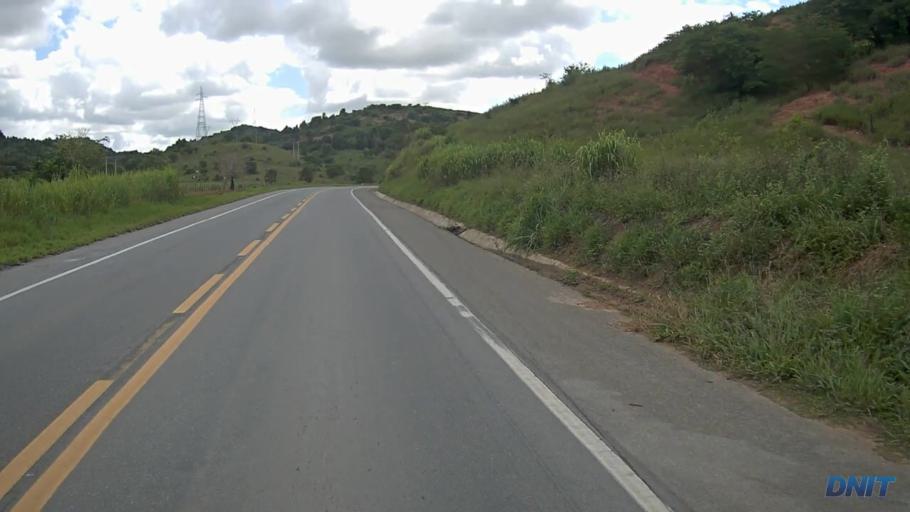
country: BR
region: Minas Gerais
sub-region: Governador Valadares
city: Governador Valadares
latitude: -18.9683
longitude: -42.0915
